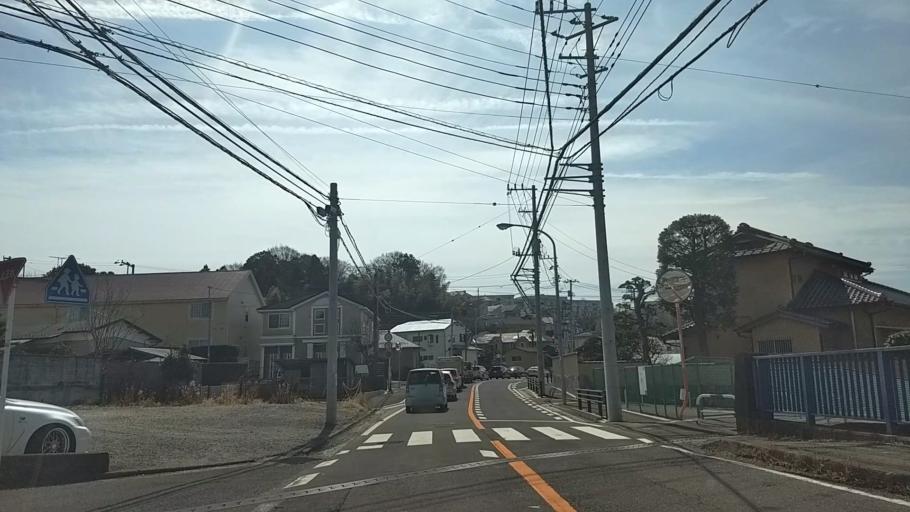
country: JP
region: Kanagawa
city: Fujisawa
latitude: 35.3853
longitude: 139.5053
